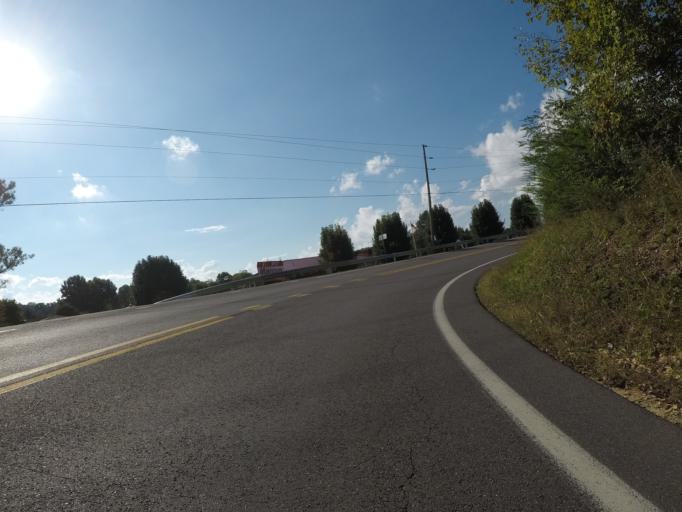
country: US
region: Ohio
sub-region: Lawrence County
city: Burlington
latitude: 38.3606
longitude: -82.5145
